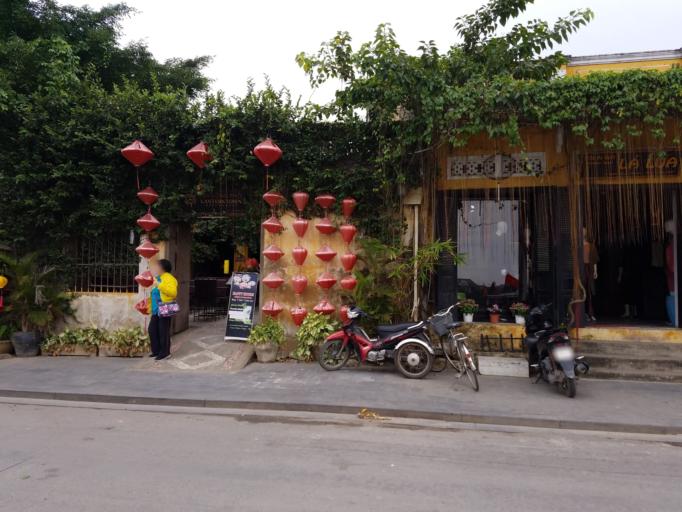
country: VN
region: Quang Nam
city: Hoi An
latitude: 15.8760
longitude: 108.3295
